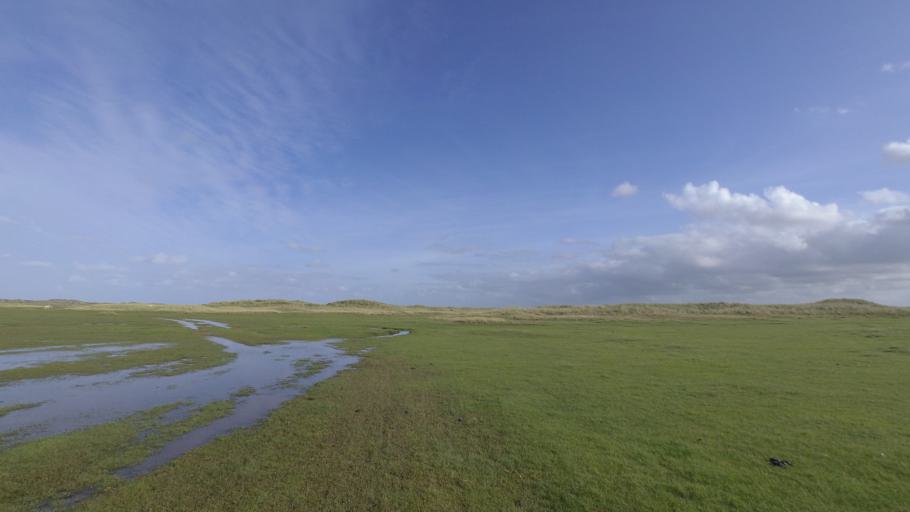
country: NL
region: Friesland
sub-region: Gemeente Ameland
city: Nes
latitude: 53.4555
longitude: 5.8670
